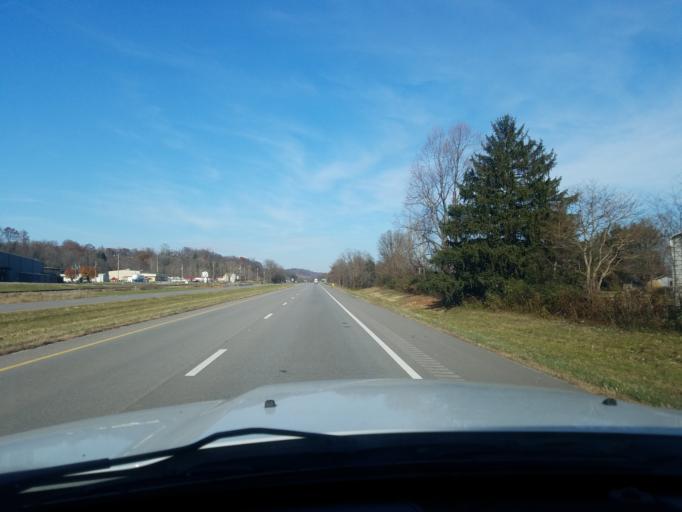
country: US
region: West Virginia
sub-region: Wood County
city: Vienna
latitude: 39.3198
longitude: -81.5633
